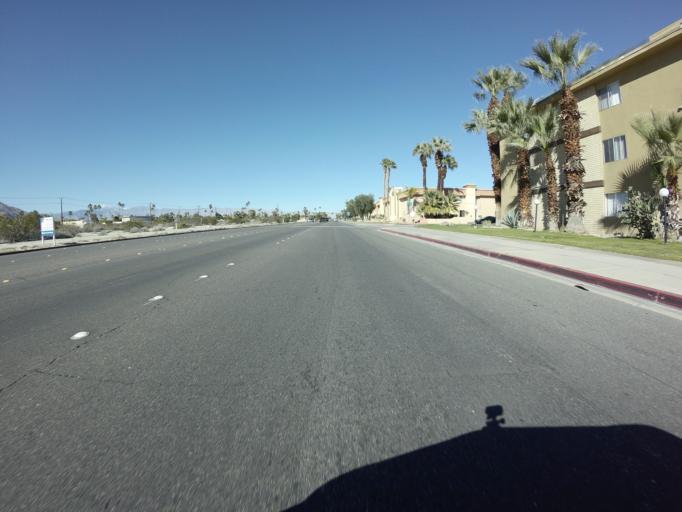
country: US
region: California
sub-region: Riverside County
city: Palm Springs
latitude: 33.8283
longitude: -116.5282
